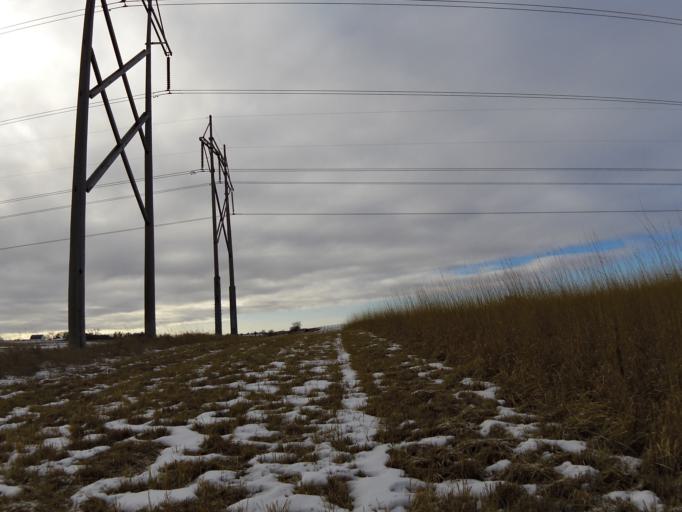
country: US
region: Wisconsin
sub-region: Pierce County
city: Prescott
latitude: 44.8022
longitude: -92.8311
